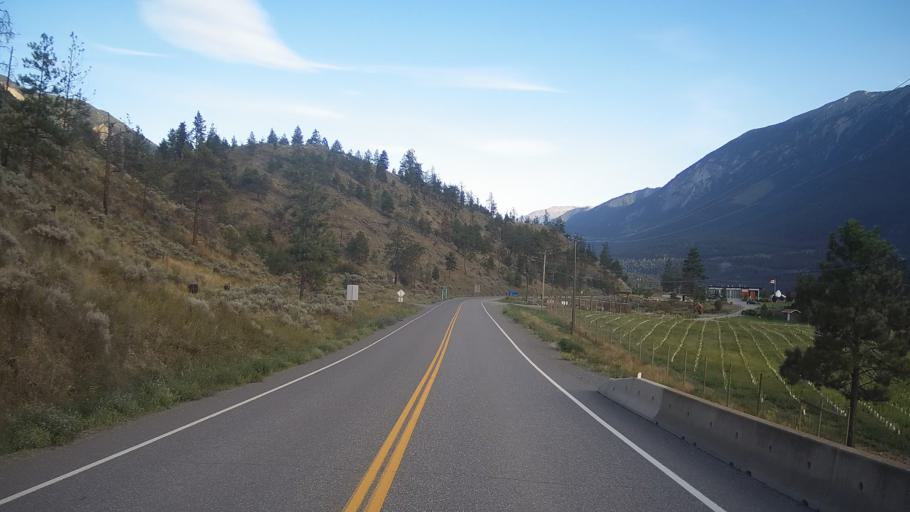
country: CA
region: British Columbia
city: Lillooet
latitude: 50.6915
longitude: -121.9206
